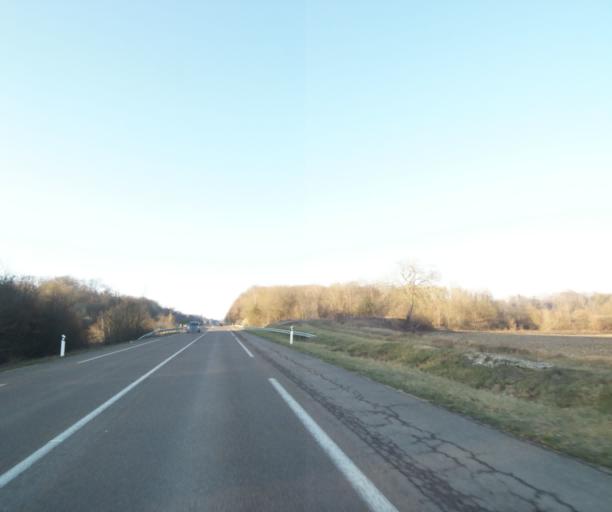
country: FR
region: Champagne-Ardenne
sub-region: Departement de la Haute-Marne
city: Chevillon
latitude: 48.5010
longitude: 5.1059
